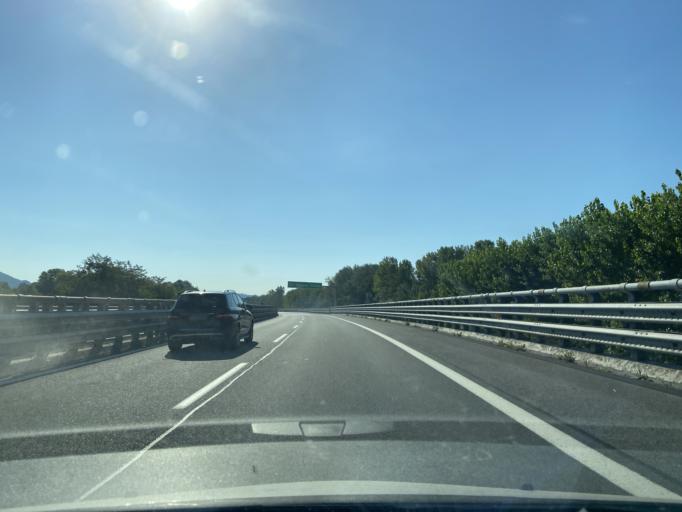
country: IT
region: Piedmont
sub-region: Provincia di Torino
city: Sant'Ambrogio di Torino
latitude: 45.0971
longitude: 7.3784
